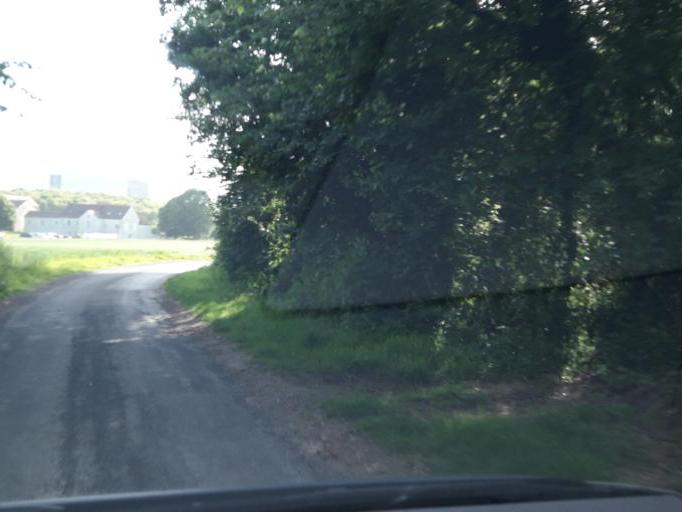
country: FR
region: Ile-de-France
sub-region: Departement de l'Essonne
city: Bondoufle
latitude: 48.5850
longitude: 2.3845
